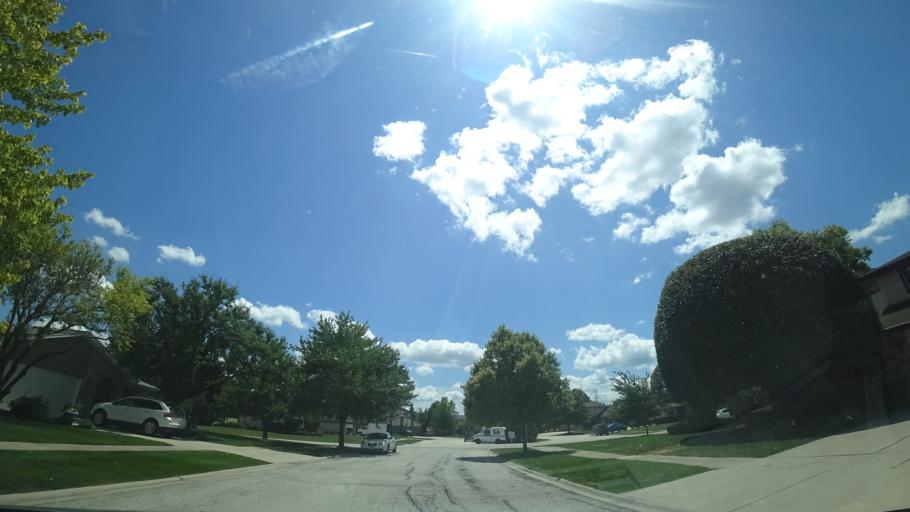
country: US
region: Illinois
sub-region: Will County
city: Homer Glen
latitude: 41.5775
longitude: -87.8940
